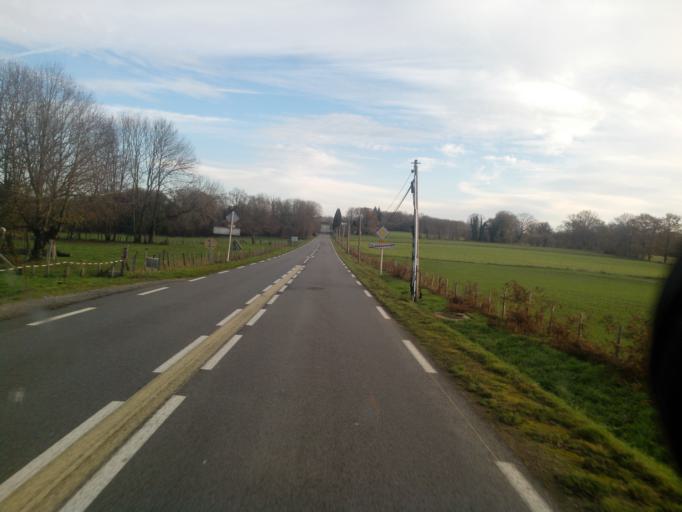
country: FR
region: Limousin
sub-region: Departement de la Haute-Vienne
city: Saint-Paul
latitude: 45.7872
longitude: 1.4705
